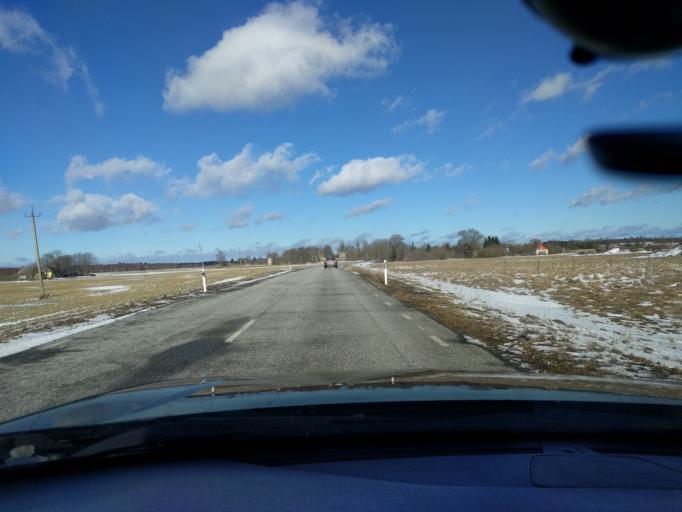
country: EE
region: Harju
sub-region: Raasiku vald
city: Raasiku
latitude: 59.3924
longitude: 25.1873
